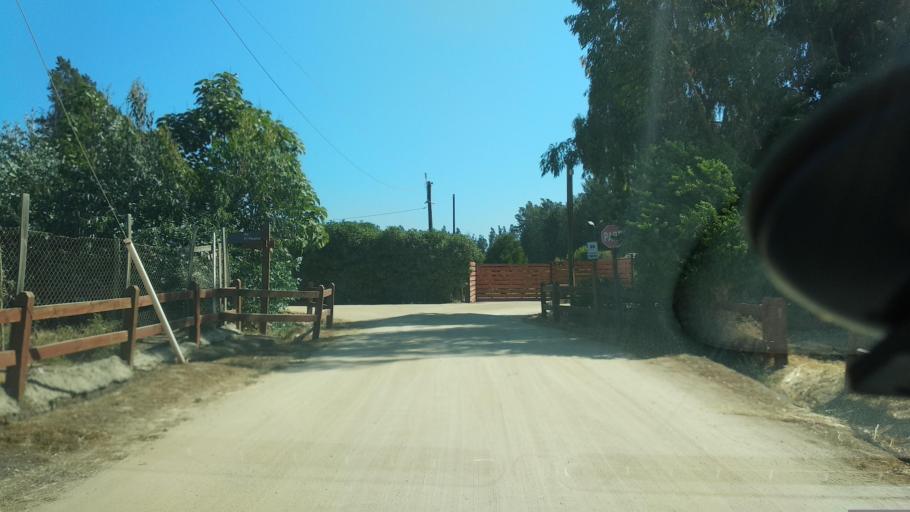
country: CL
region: Valparaiso
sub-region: Provincia de Marga Marga
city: Limache
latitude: -32.9740
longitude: -71.3102
